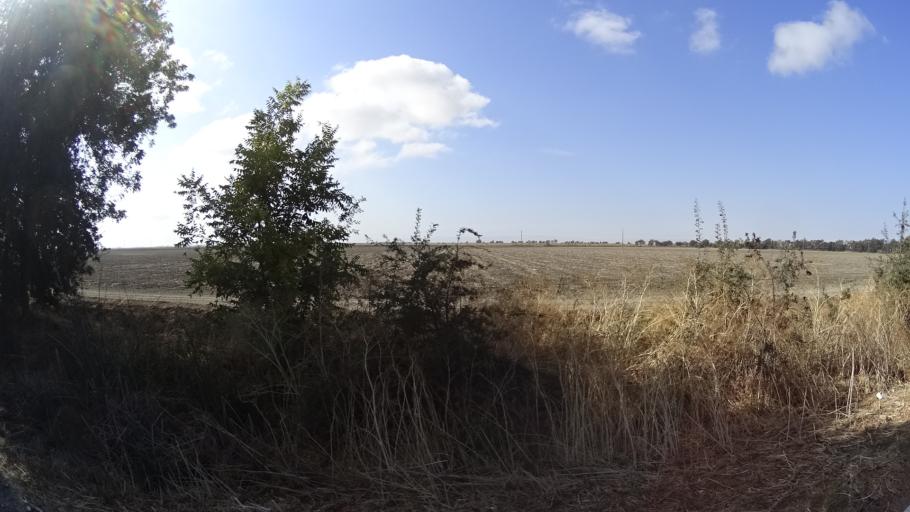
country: US
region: California
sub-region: Yolo County
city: Woodland
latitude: 38.8500
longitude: -121.7790
